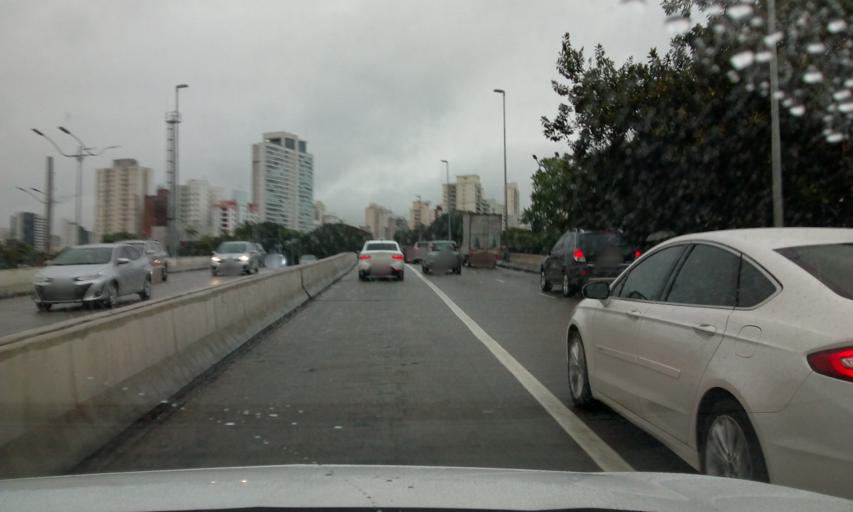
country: BR
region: Sao Paulo
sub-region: Sao Paulo
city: Sao Paulo
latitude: -23.6079
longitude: -46.6765
